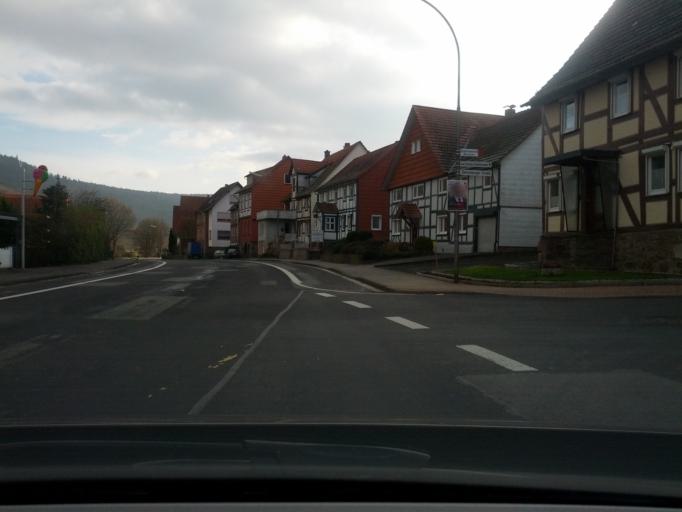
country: DE
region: Lower Saxony
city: Buhren
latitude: 51.4787
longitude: 9.6193
